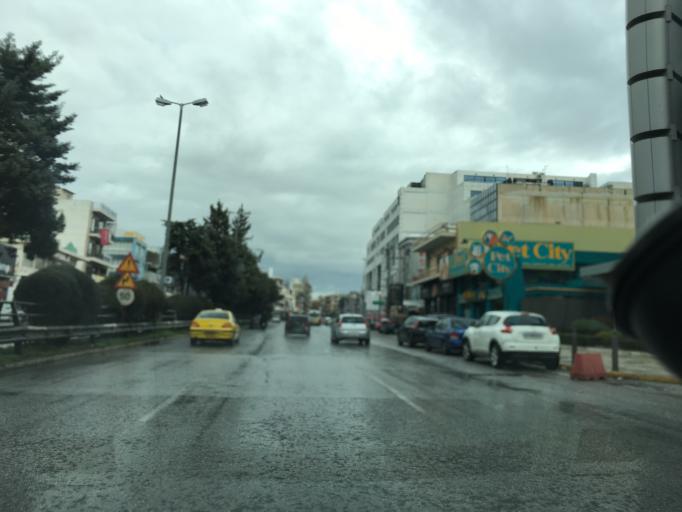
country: GR
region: Attica
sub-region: Nomarchia Athinas
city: Marousi
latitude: 38.0474
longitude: 23.8078
